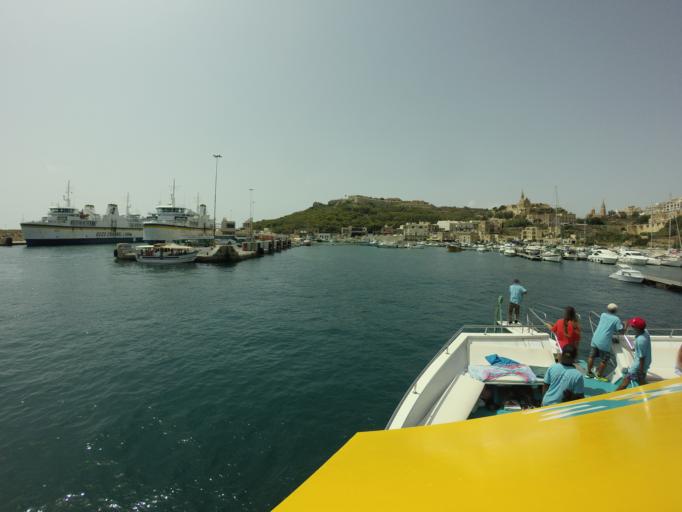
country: MT
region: Ghajnsielem
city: Mgarr
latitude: 36.0255
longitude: 14.2993
